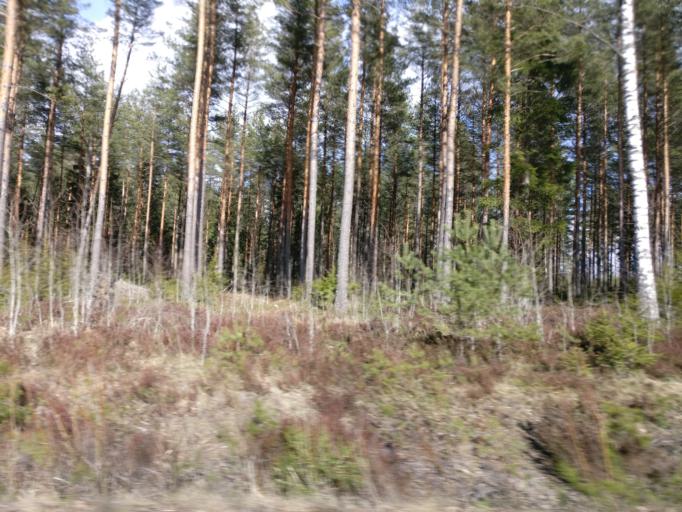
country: FI
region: Uusimaa
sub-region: Helsinki
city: Sammatti
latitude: 60.2771
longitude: 23.7778
